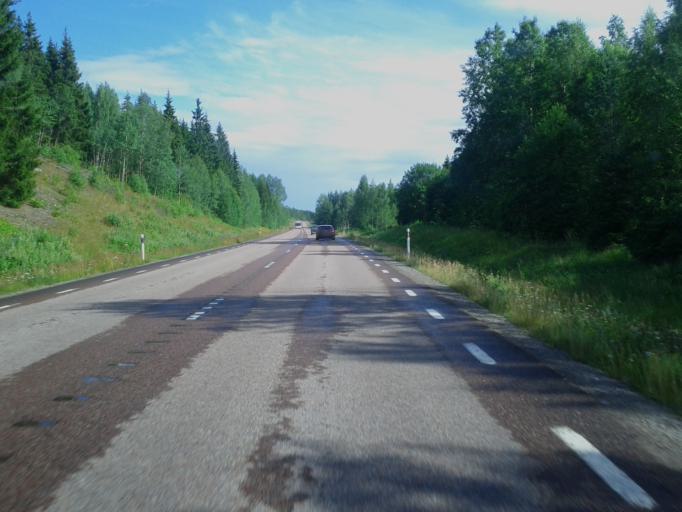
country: SE
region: Dalarna
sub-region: Faluns Kommun
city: Falun
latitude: 60.6515
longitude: 15.5600
